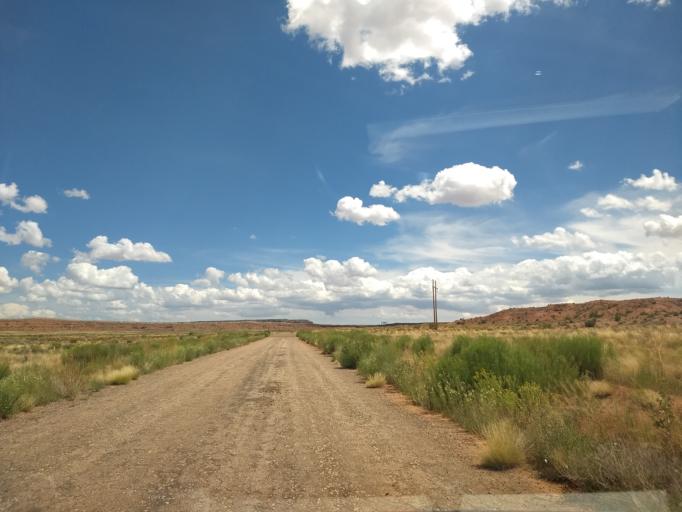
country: US
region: Arizona
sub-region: Coconino County
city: Fredonia
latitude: 36.9443
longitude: -112.5055
